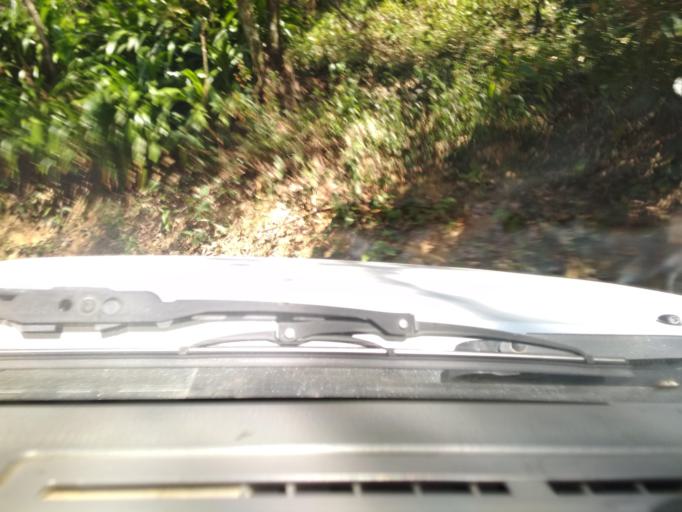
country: MX
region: Veracruz
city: Tequila
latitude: 18.7524
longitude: -97.0918
